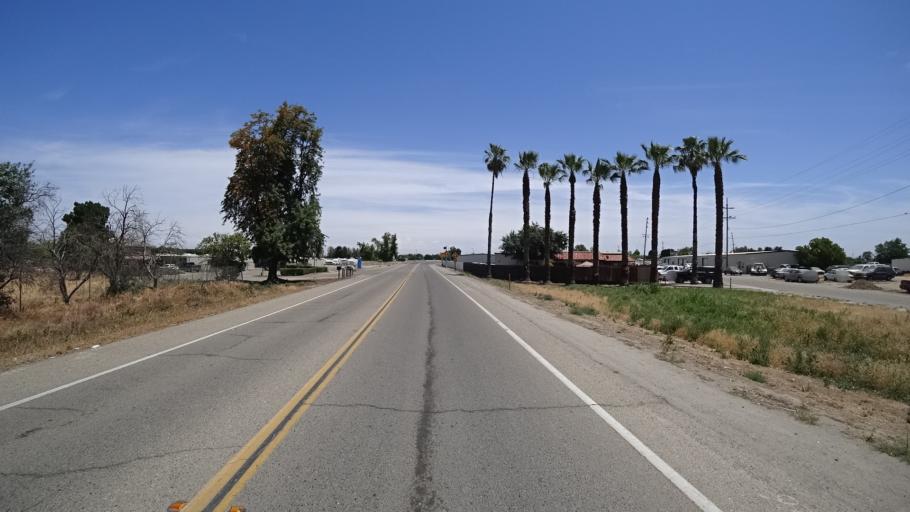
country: US
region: California
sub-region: Kings County
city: Armona
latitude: 36.3138
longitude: -119.6976
